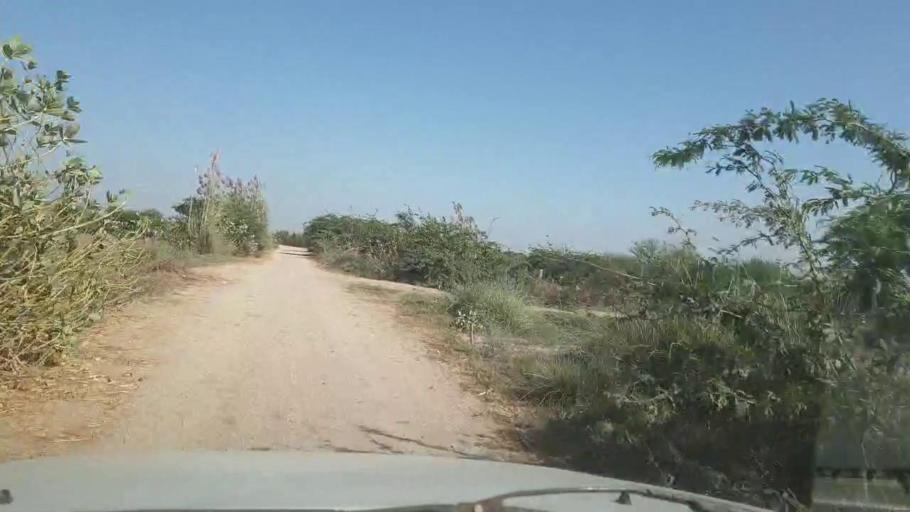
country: PK
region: Sindh
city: Mirpur Sakro
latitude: 24.4653
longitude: 67.7697
